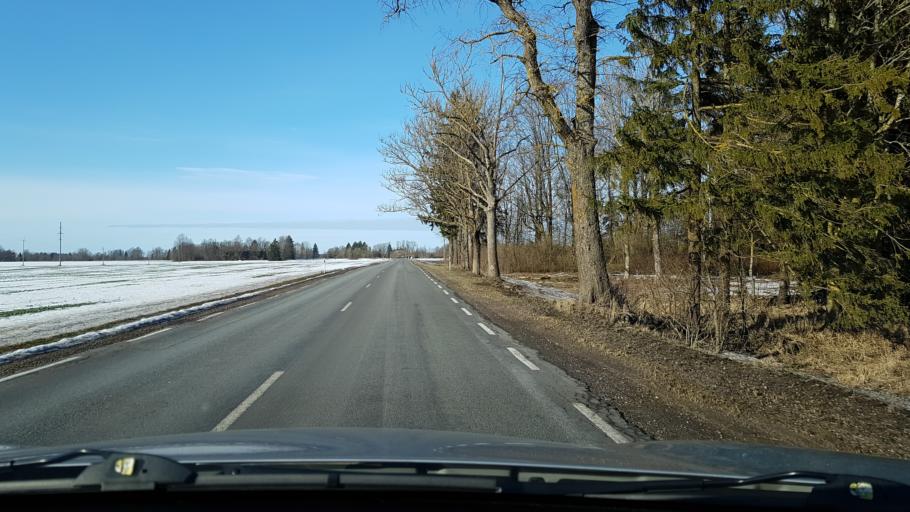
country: EE
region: Viljandimaa
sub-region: Vohma linn
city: Vohma
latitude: 58.6300
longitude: 25.6208
